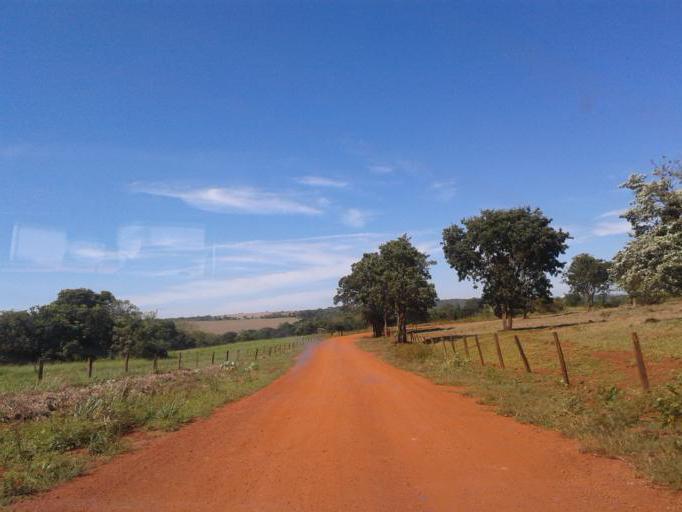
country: BR
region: Minas Gerais
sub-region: Capinopolis
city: Capinopolis
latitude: -18.6654
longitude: -49.5915
